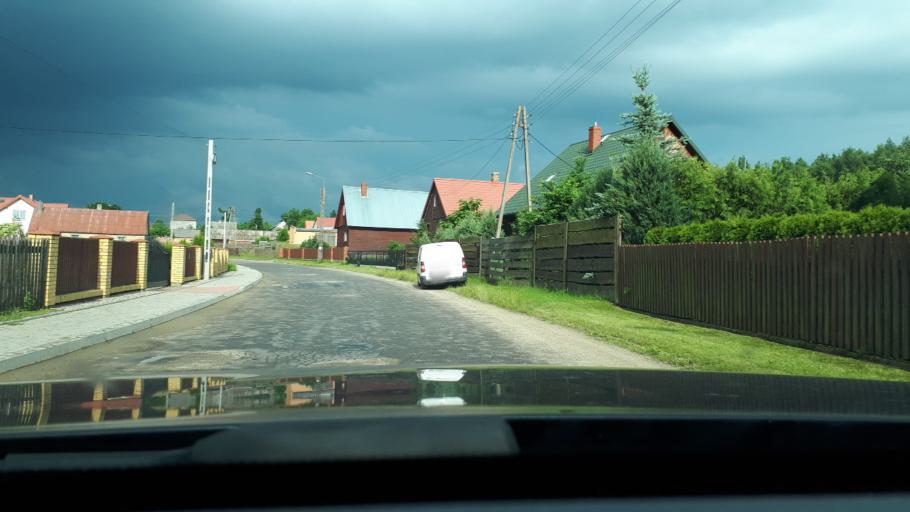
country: PL
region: Podlasie
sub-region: Powiat moniecki
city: Knyszyn
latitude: 53.2730
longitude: 22.9804
